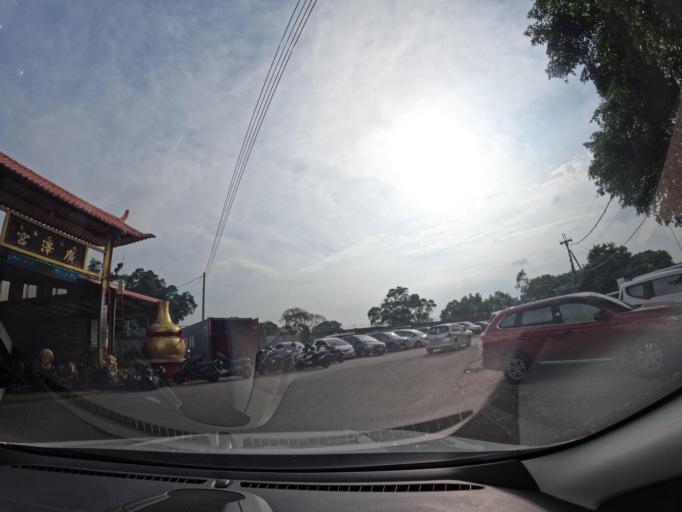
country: TW
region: Taiwan
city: Daxi
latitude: 24.9285
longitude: 121.3042
